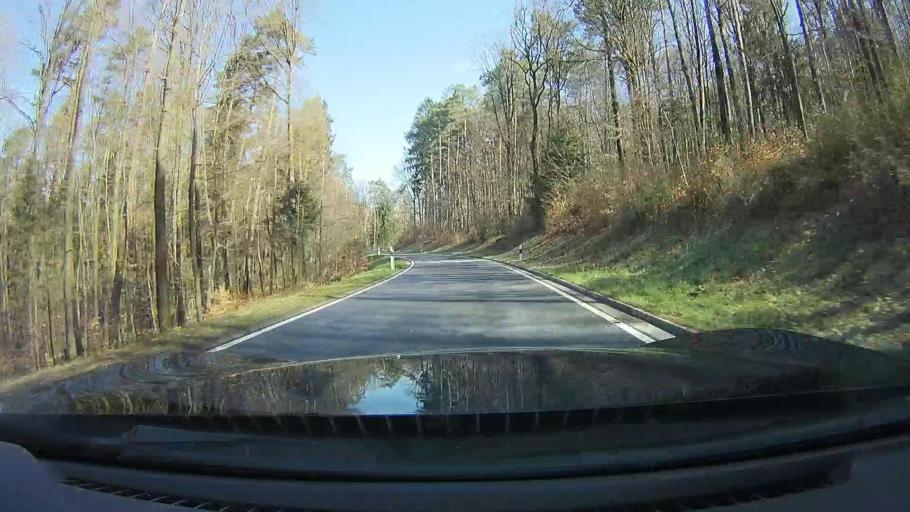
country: DE
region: Hesse
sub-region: Regierungsbezirk Darmstadt
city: Rothenberg
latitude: 49.5147
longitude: 8.9211
